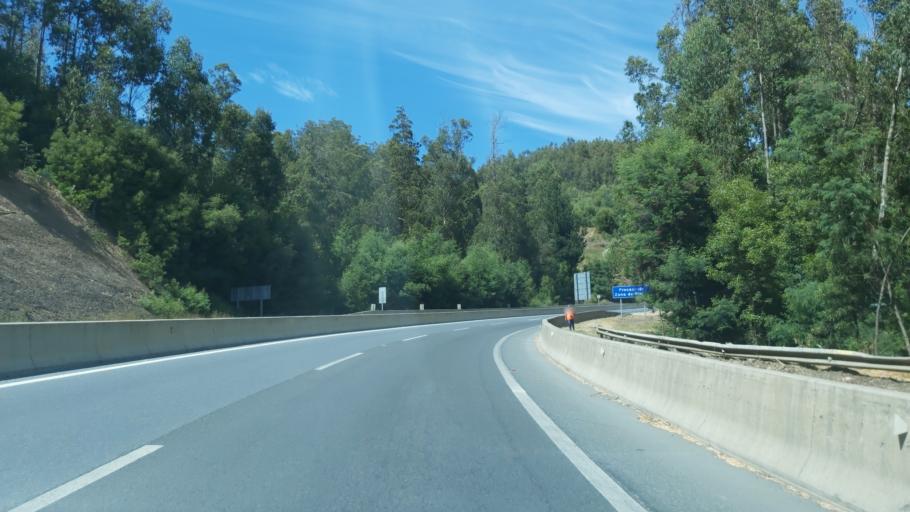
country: CL
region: Biobio
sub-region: Provincia de Concepcion
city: Lota
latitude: -37.1181
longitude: -73.1478
